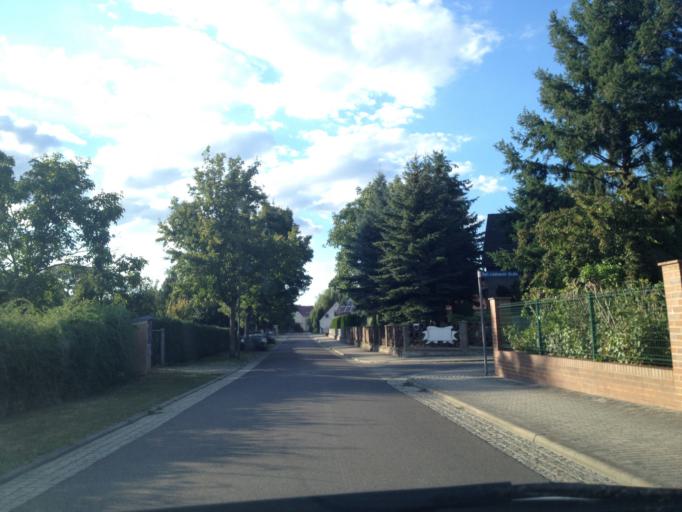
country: DE
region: Brandenburg
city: Vetschau
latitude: 51.7868
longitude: 14.0740
